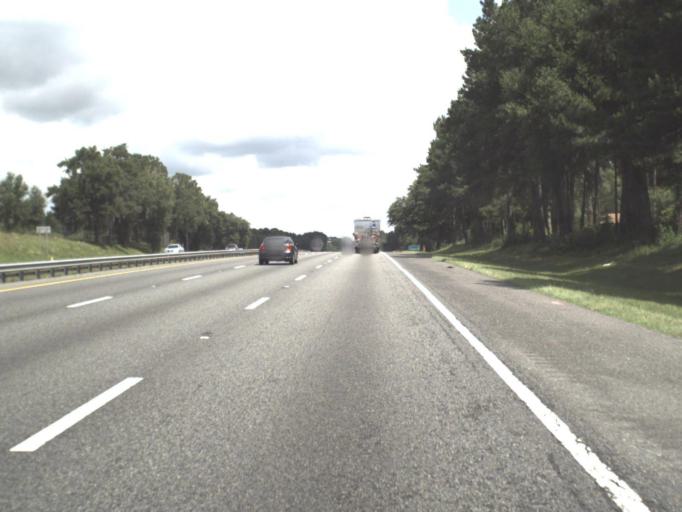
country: US
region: Florida
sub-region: Columbia County
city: Lake City
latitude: 30.1880
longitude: -82.6926
